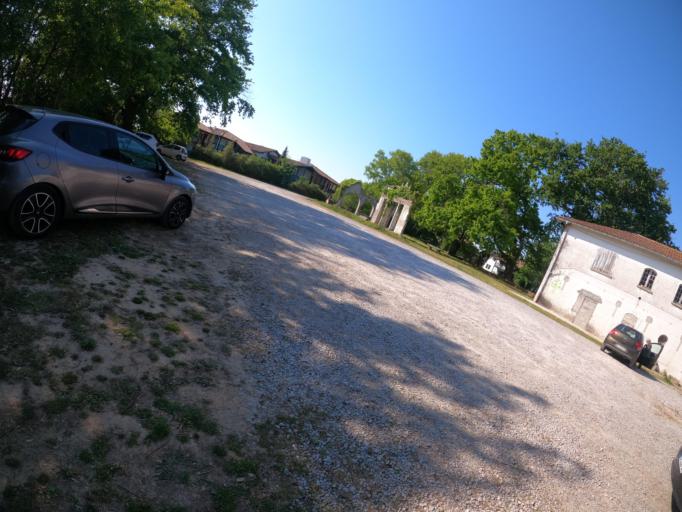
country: FR
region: Aquitaine
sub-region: Departement des Pyrenees-Atlantiques
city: Arcangues
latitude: 43.4364
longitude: -1.5230
